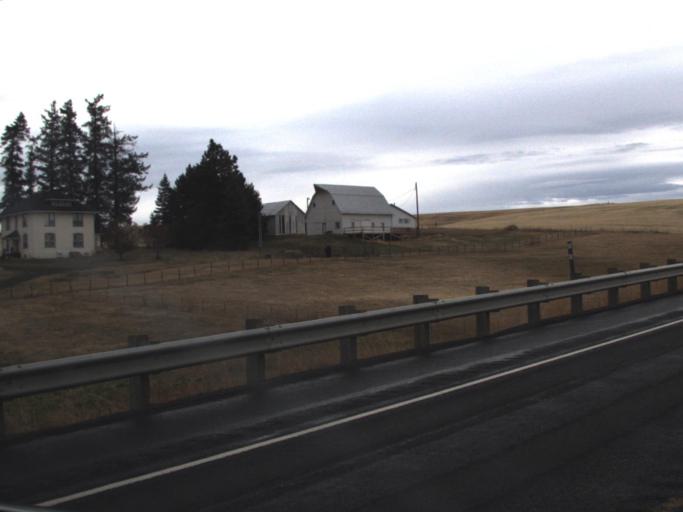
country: US
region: Washington
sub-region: Asotin County
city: Clarkston
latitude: 46.5274
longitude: -117.0843
